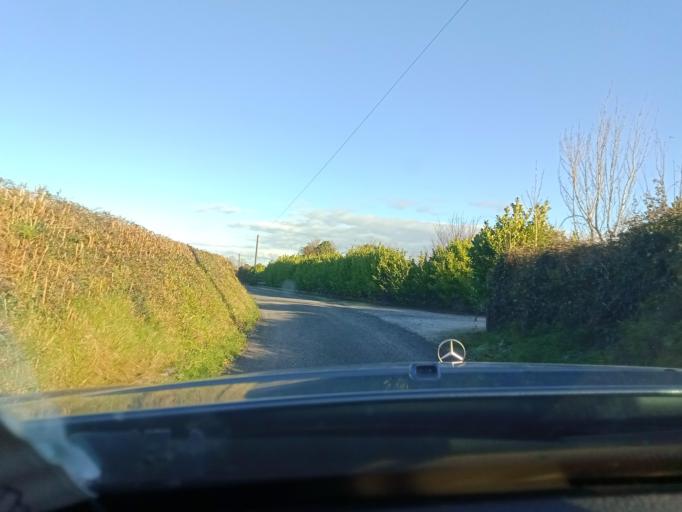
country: IE
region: Leinster
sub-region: Kilkenny
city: Graiguenamanagh
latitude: 52.5525
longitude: -6.9491
